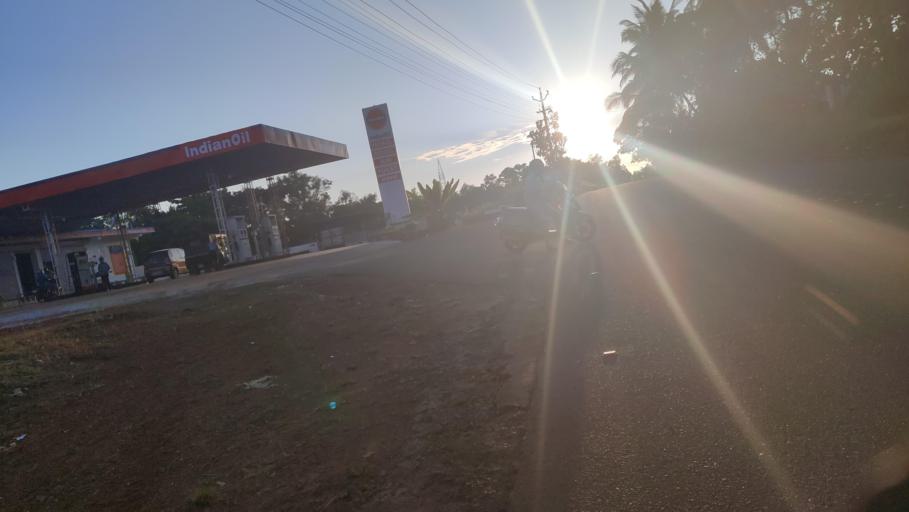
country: IN
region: Kerala
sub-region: Kasaragod District
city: Kannangad
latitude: 12.4039
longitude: 75.0959
